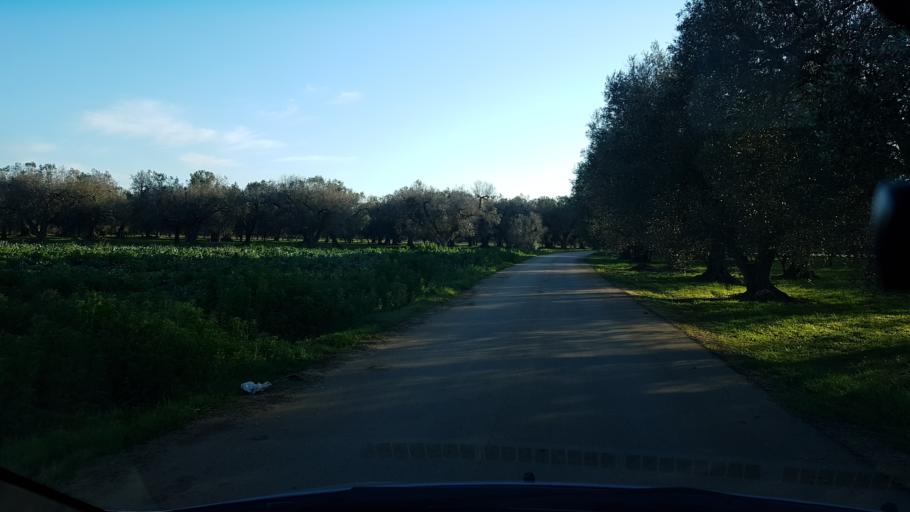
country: IT
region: Apulia
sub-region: Provincia di Brindisi
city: Mesagne
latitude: 40.5633
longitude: 17.8678
